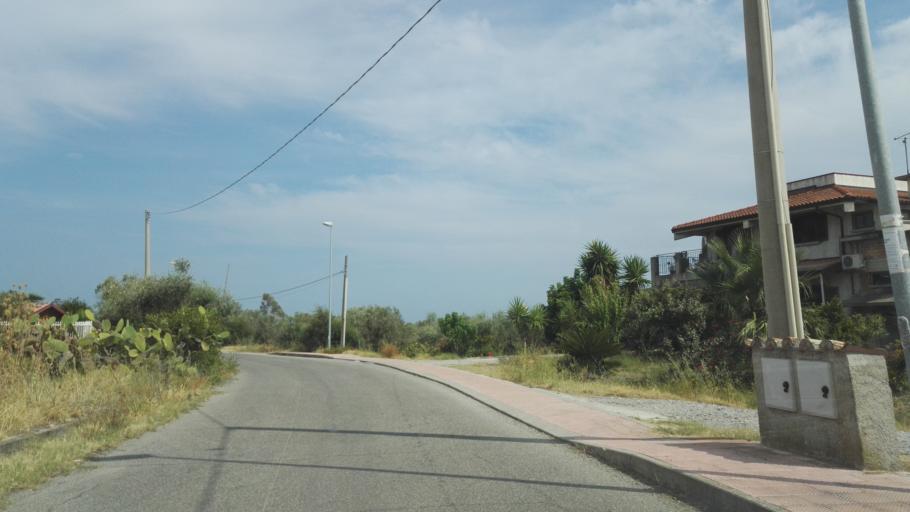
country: IT
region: Calabria
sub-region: Provincia di Reggio Calabria
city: Monasterace Marina
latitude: 38.4264
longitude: 16.5468
